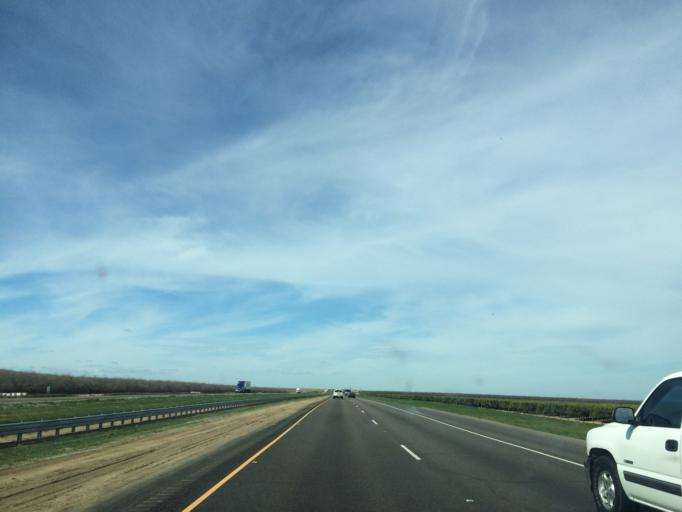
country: US
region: California
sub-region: Merced County
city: South Dos Palos
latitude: 36.7067
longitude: -120.6741
